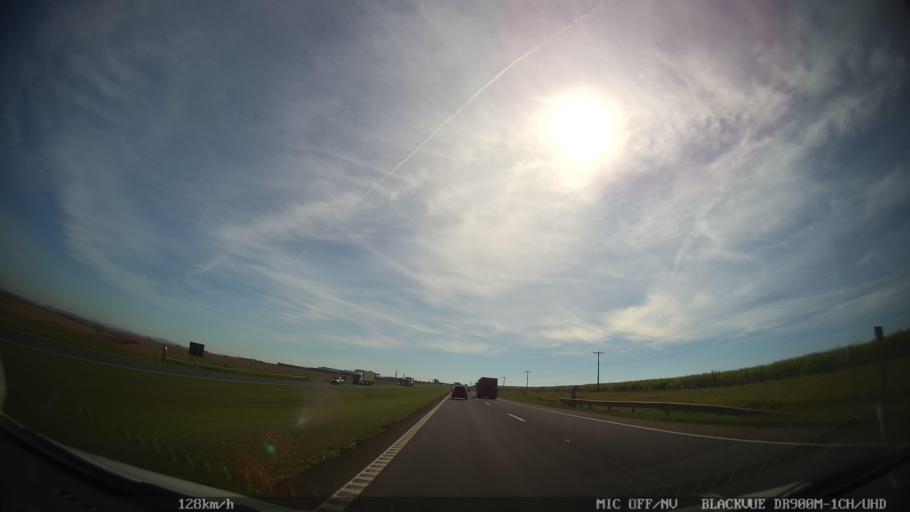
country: BR
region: Sao Paulo
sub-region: Araras
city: Araras
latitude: -22.4261
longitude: -47.3932
